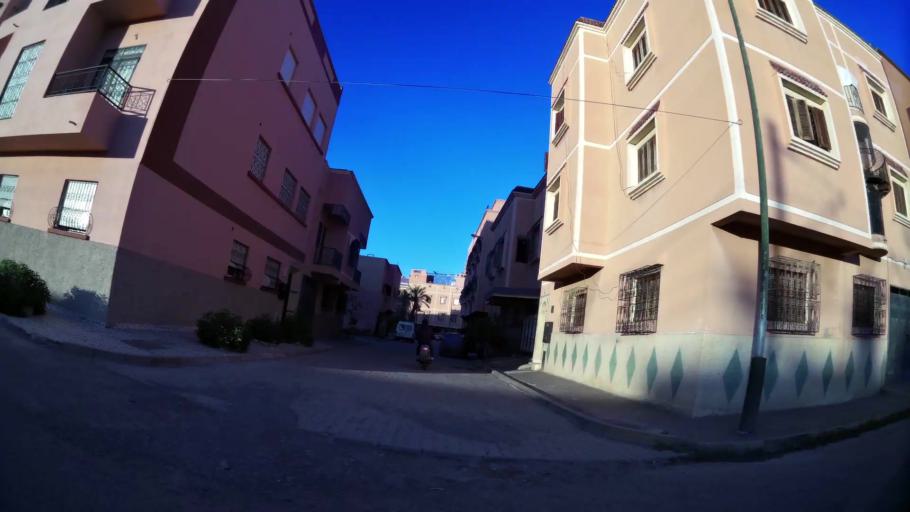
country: MA
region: Marrakech-Tensift-Al Haouz
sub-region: Marrakech
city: Marrakesh
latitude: 31.6375
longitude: -8.0384
